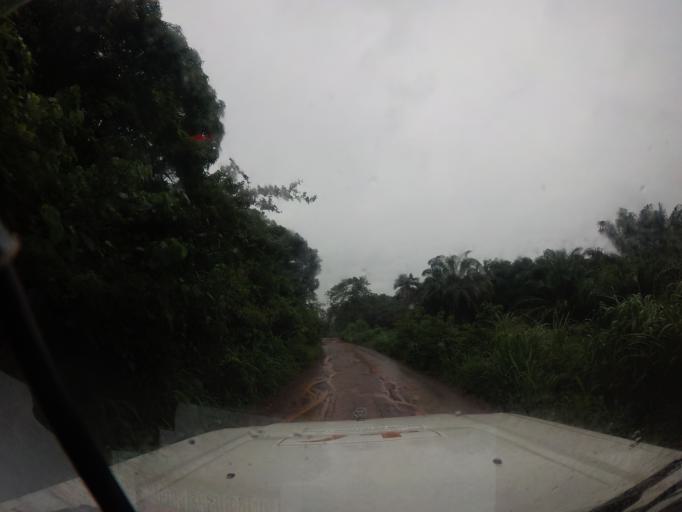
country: SL
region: Northern Province
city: Kabala
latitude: 9.6258
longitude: -11.5505
